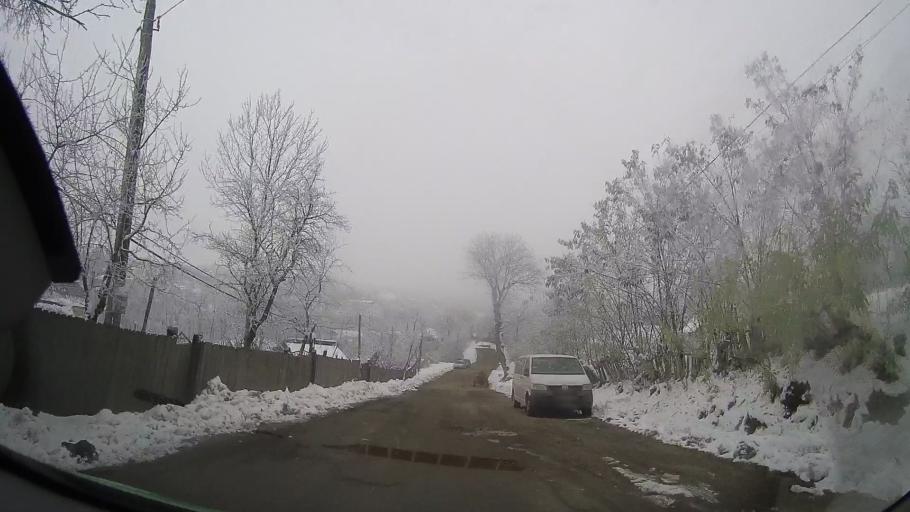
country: RO
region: Iasi
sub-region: Comuna Tansa
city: Tansa
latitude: 46.9086
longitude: 27.2394
